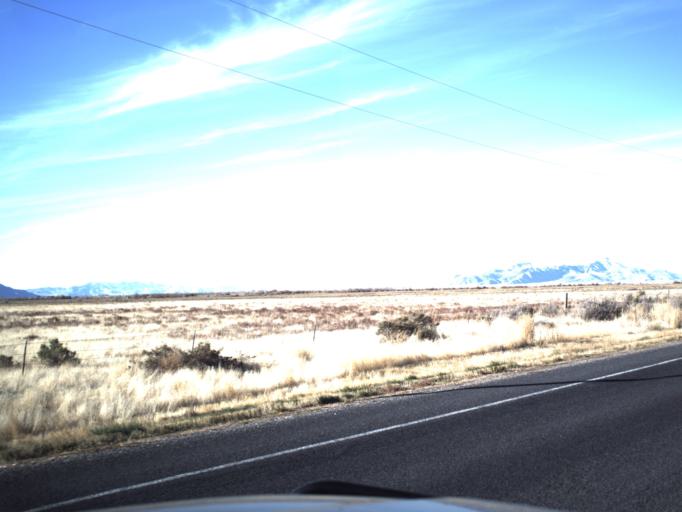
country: US
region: Utah
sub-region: Tooele County
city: Erda
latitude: 40.6101
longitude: -112.3709
